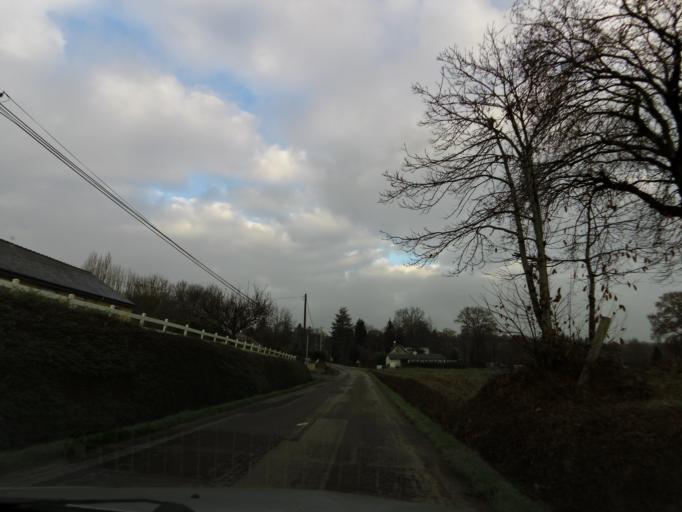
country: FR
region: Brittany
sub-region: Departement d'Ille-et-Vilaine
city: Orgeres
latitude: 47.9721
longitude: -1.6480
